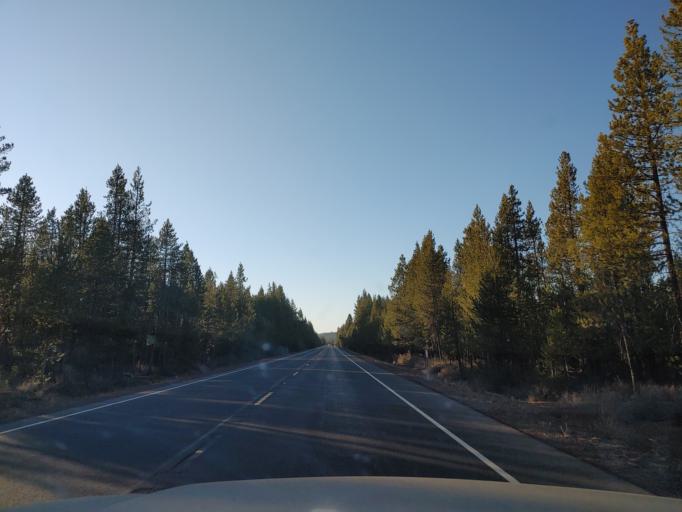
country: US
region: Oregon
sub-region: Deschutes County
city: La Pine
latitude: 43.4090
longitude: -121.8296
